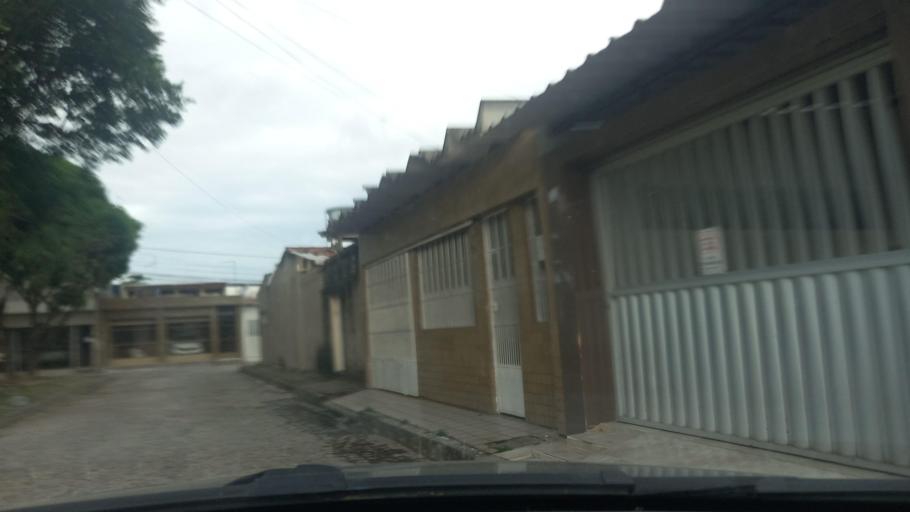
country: BR
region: Pernambuco
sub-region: Recife
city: Recife
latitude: -8.1156
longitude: -34.9194
